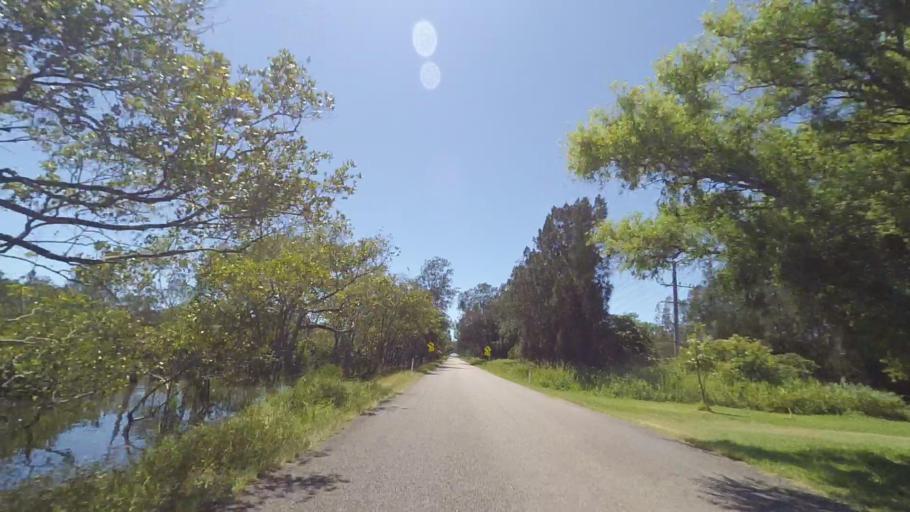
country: AU
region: New South Wales
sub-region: Port Stephens Shire
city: Medowie
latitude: -32.7802
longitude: 151.9526
